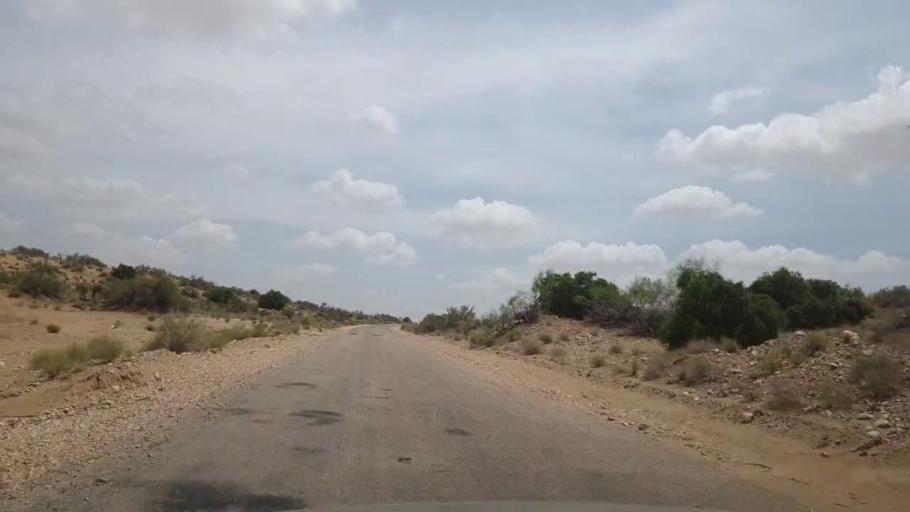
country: PK
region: Sindh
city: Kot Diji
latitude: 27.1625
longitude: 69.2232
